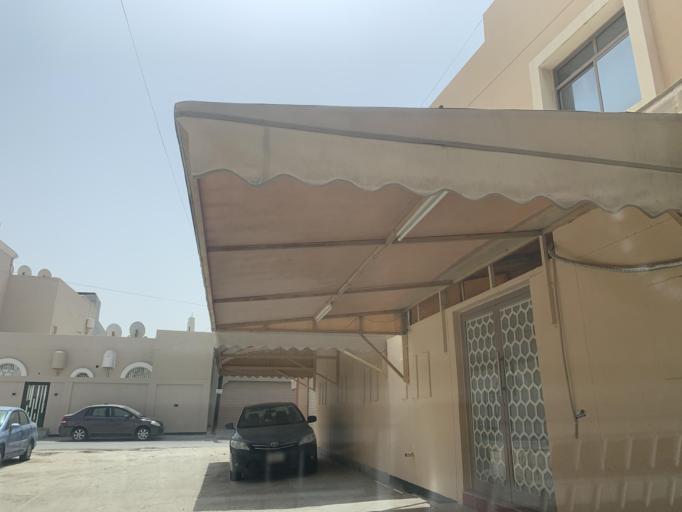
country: BH
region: Northern
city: Madinat `Isa
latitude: 26.1776
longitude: 50.5555
